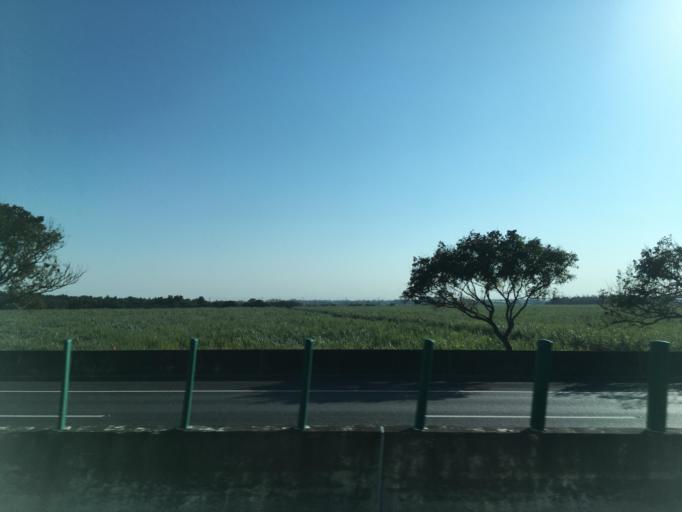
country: TW
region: Taiwan
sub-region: Chiayi
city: Taibao
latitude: 23.4271
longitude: 120.3456
